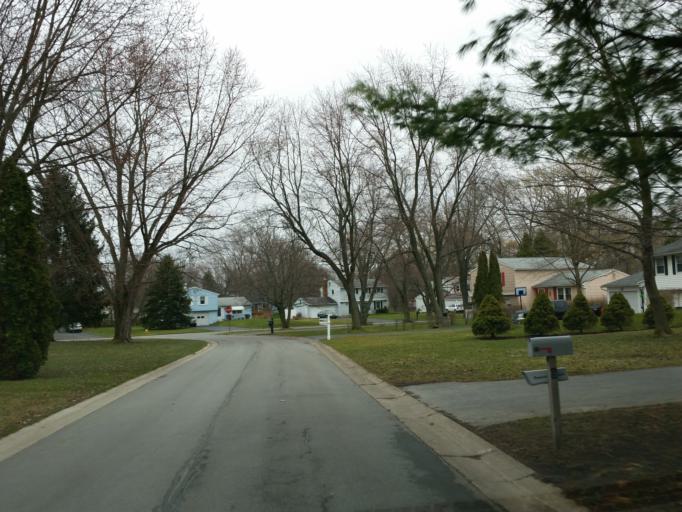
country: US
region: New York
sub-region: Monroe County
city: Scottsville
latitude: 43.1093
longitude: -77.7602
